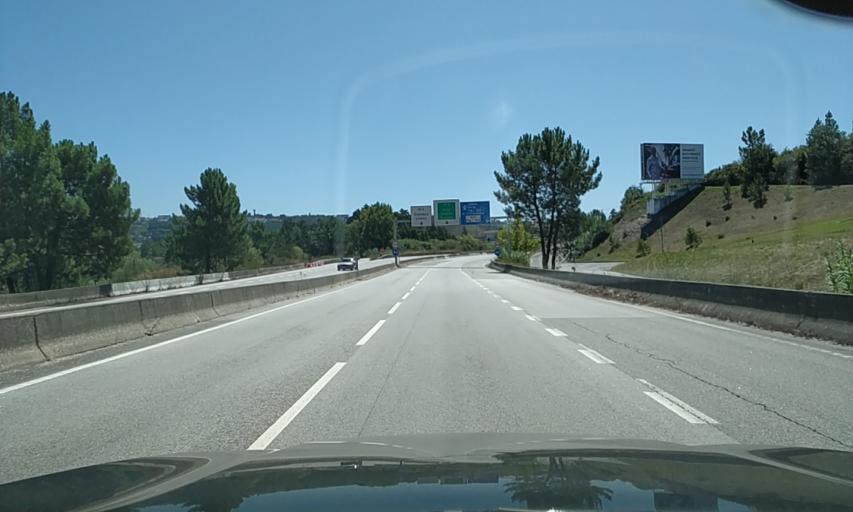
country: PT
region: Aveiro
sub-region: Mealhada
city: Pampilhosa do Botao
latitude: 40.2761
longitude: -8.4447
